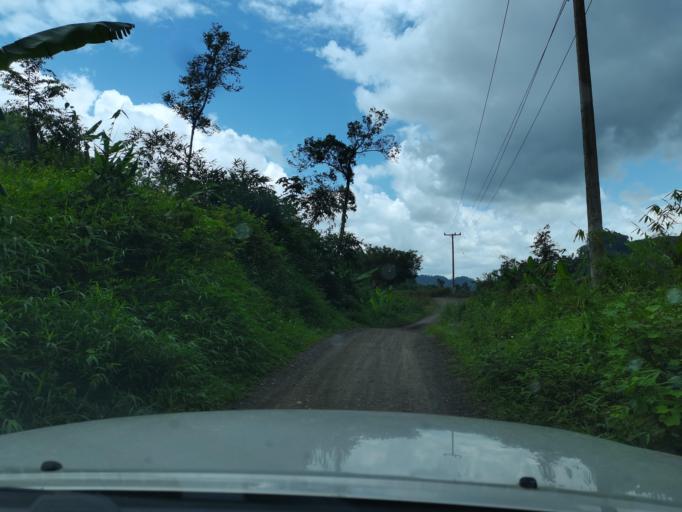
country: LA
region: Loungnamtha
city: Muang Long
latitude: 20.7732
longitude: 101.0167
